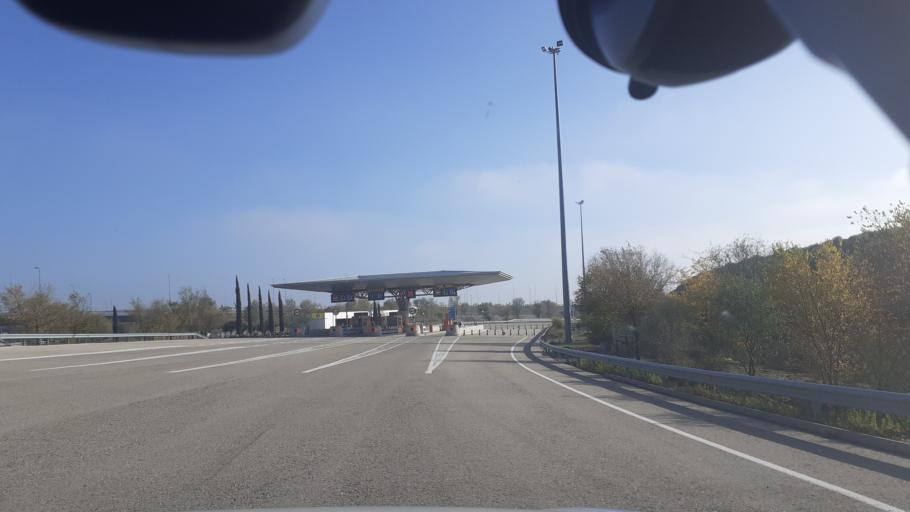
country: ES
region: Madrid
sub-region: Provincia de Madrid
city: Vicalvaro
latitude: 40.4034
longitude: -3.5780
